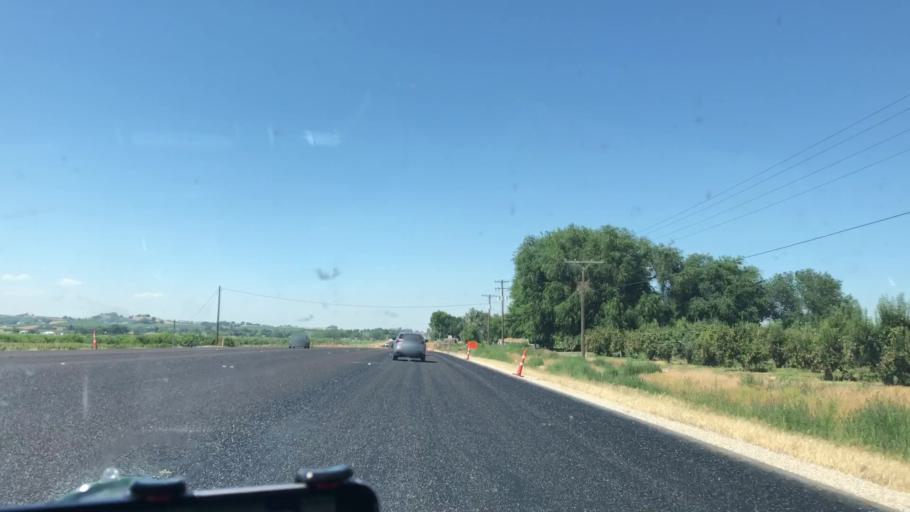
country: US
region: Idaho
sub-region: Owyhee County
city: Marsing
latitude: 43.5694
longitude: -116.7924
